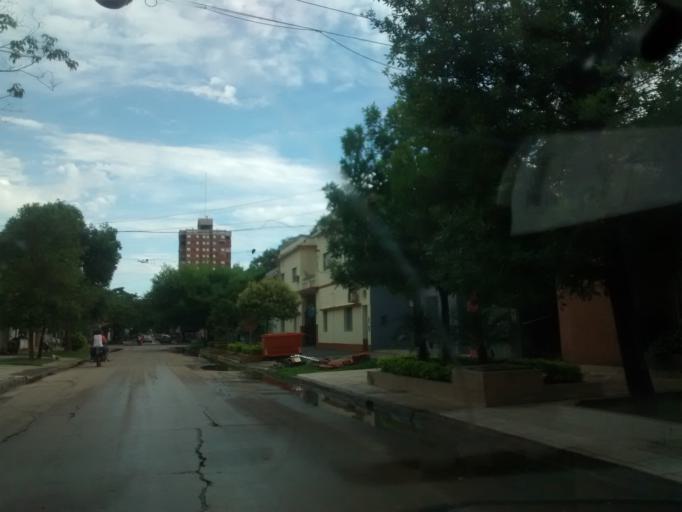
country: AR
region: Chaco
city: Resistencia
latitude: -27.4474
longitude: -58.9925
